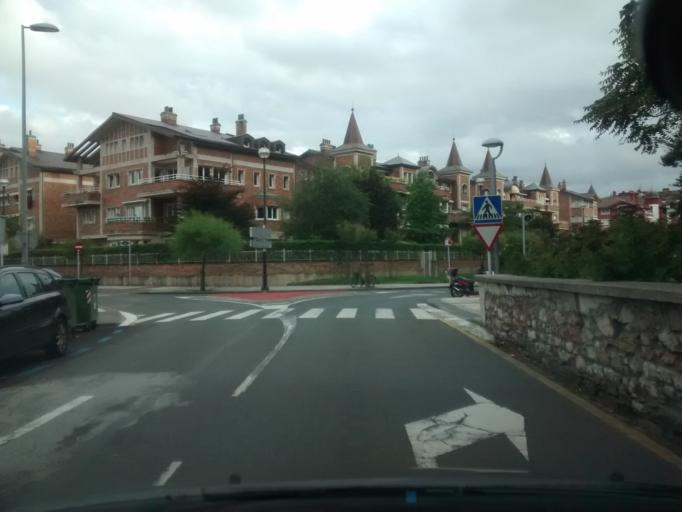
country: ES
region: Basque Country
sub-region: Provincia de Guipuzcoa
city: San Sebastian
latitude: 43.3170
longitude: -2.0057
